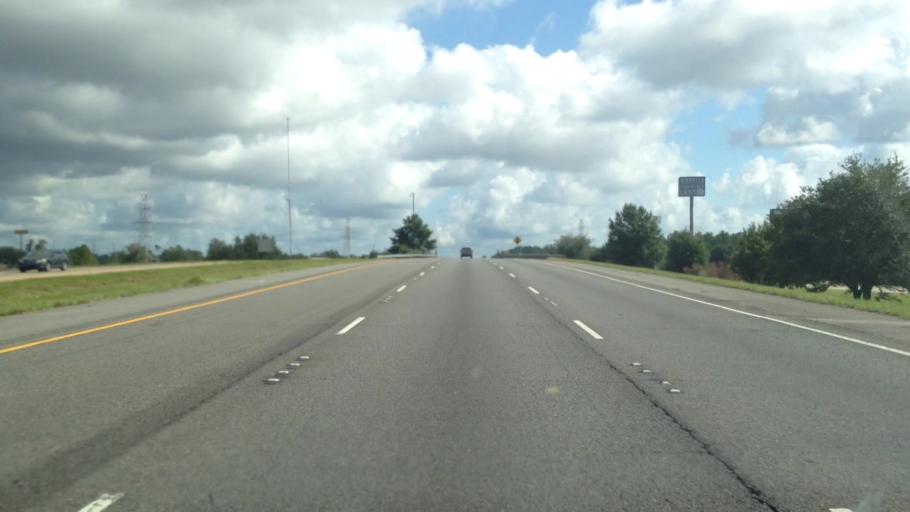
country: US
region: Louisiana
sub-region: Saint Tammany Parish
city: Slidell
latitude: 30.2454
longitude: -89.7641
